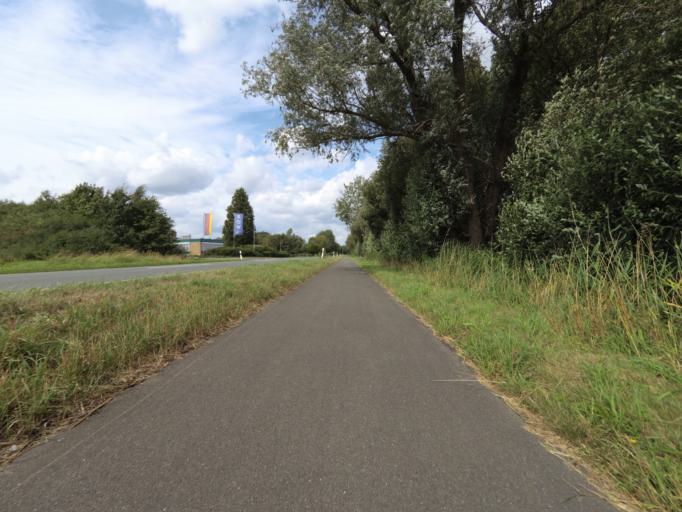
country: DE
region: North Rhine-Westphalia
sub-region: Regierungsbezirk Munster
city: Gronau
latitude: 52.1561
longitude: 6.9860
